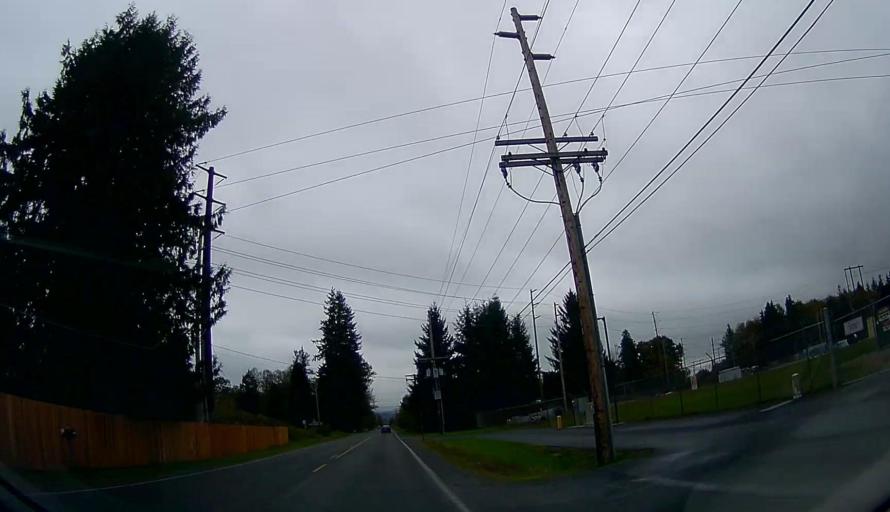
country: US
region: Washington
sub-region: Skagit County
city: Sedro-Woolley
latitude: 48.5066
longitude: -122.2060
